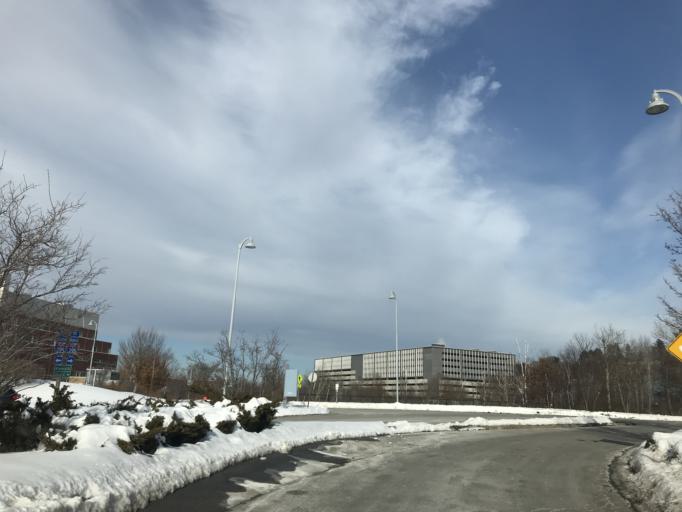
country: US
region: Maine
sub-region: Cumberland County
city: Portland
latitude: 43.6465
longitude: -70.2815
